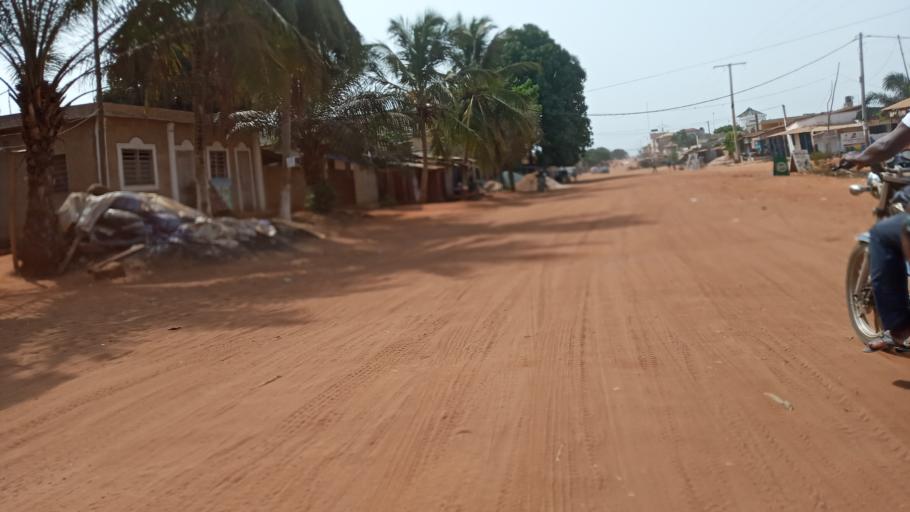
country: TG
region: Maritime
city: Lome
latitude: 6.2070
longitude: 1.1621
